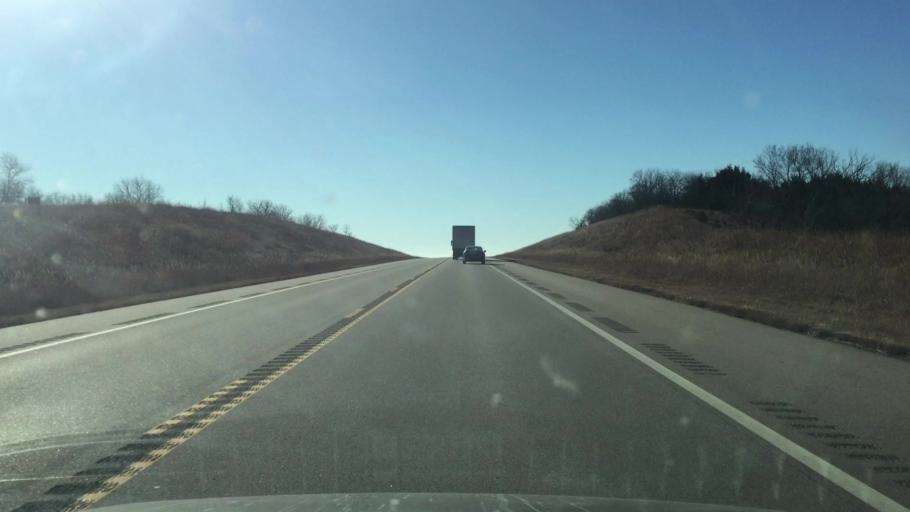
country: US
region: Kansas
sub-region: Allen County
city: Iola
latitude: 38.0140
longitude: -95.3807
